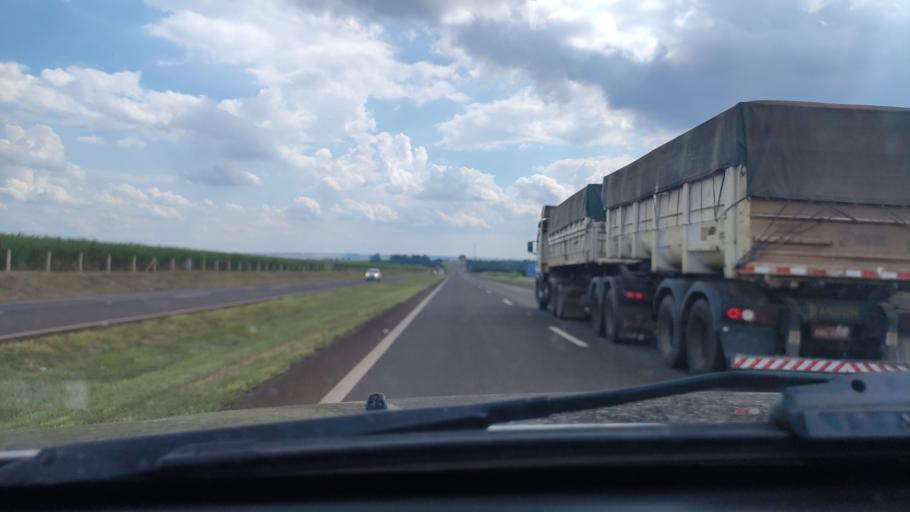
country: BR
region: Sao Paulo
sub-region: Itapui
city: Itapui
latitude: -22.3083
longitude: -48.6725
